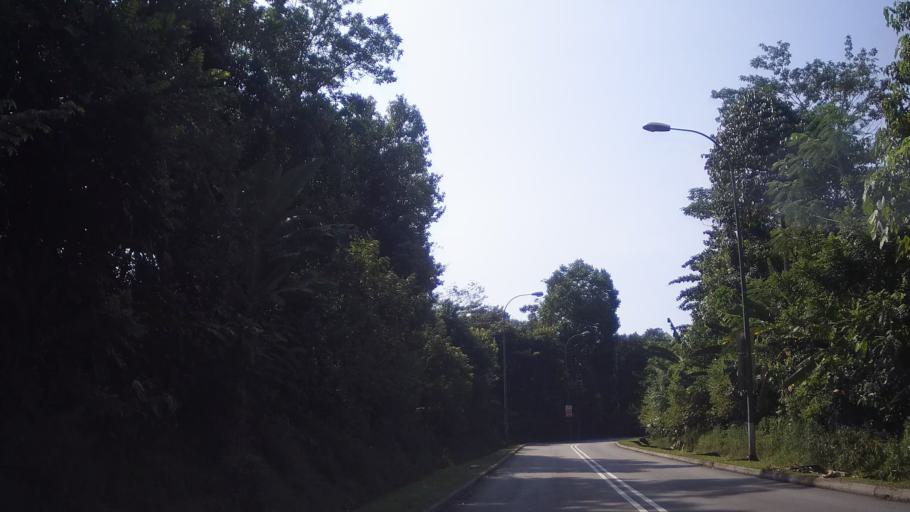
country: MY
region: Johor
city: Johor Bahru
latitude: 1.3721
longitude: 103.7775
